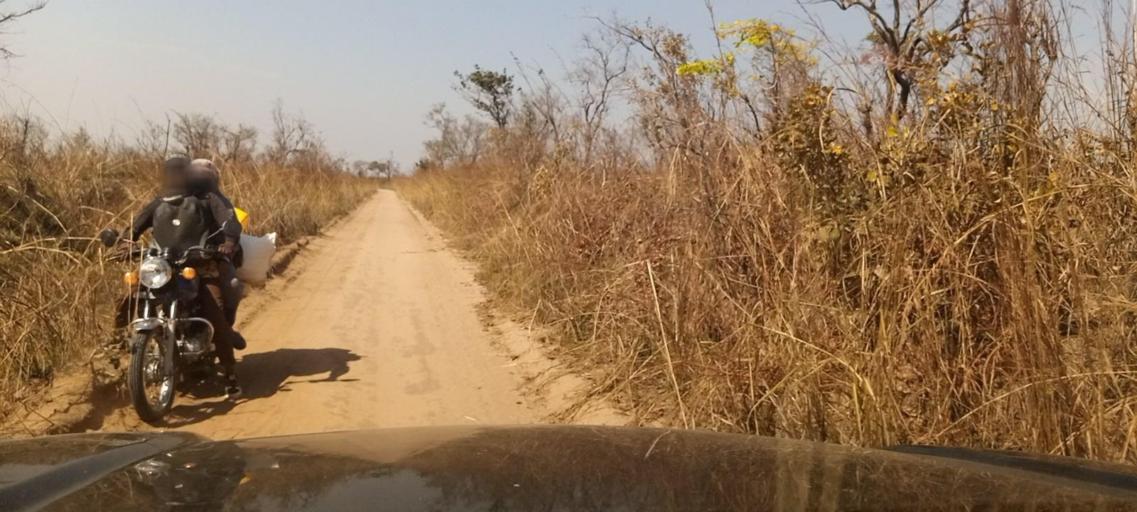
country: CD
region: Kasai-Oriental
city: Kabinda
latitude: -5.7923
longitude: 25.0439
